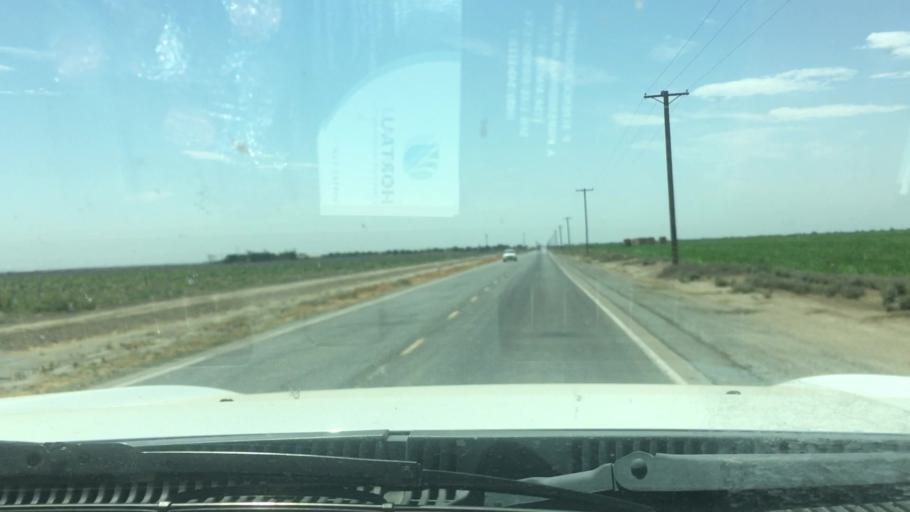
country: US
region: California
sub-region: Tulare County
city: Tipton
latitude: 36.0510
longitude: -119.4321
